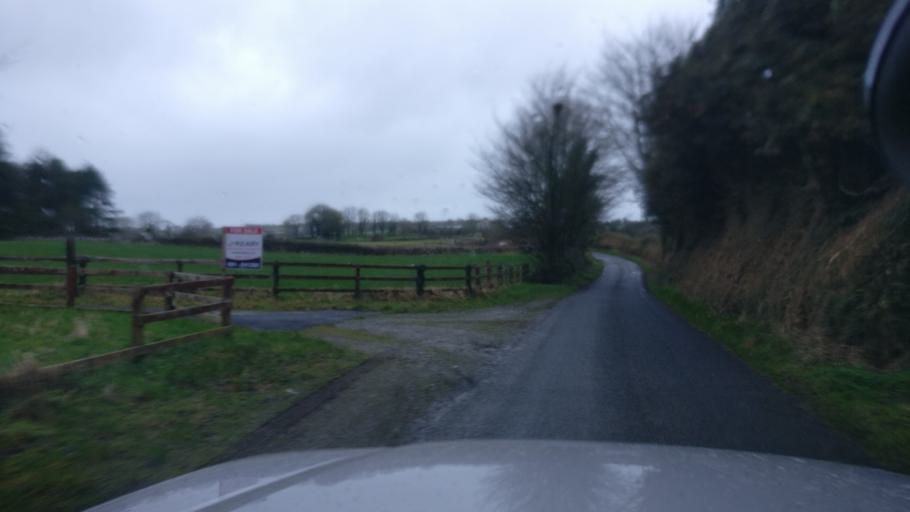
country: IE
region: Connaught
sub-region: County Galway
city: Loughrea
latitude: 53.1980
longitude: -8.6443
